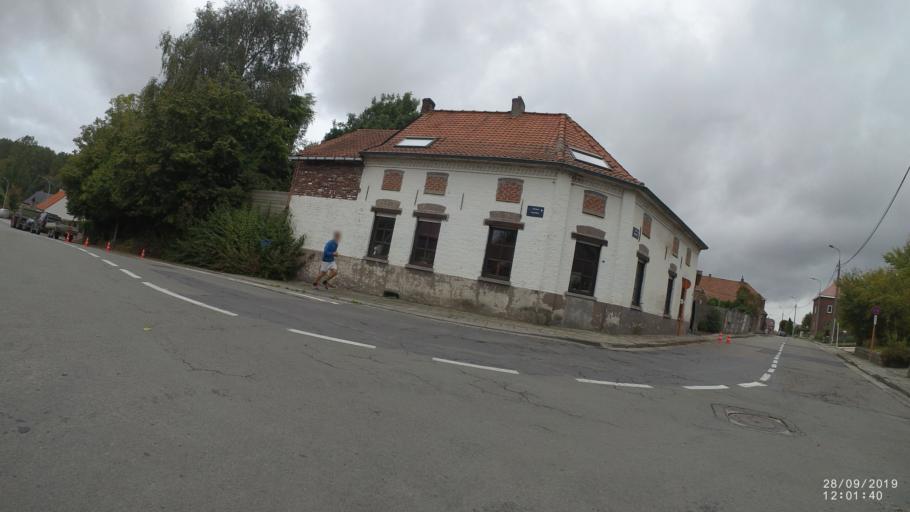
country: BE
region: Flanders
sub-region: Provincie Oost-Vlaanderen
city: Zottegem
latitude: 50.8608
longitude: 3.7967
